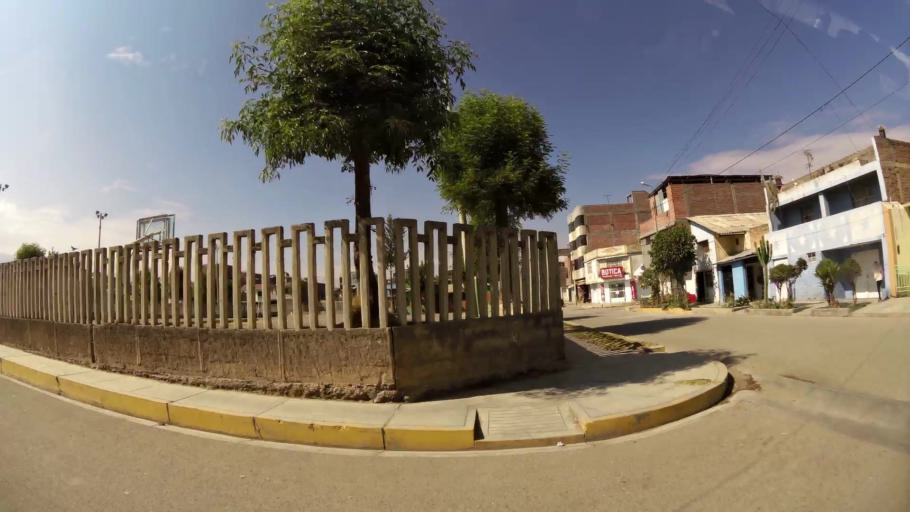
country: PE
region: Junin
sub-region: Provincia de Huancayo
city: El Tambo
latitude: -12.0736
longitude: -75.2274
